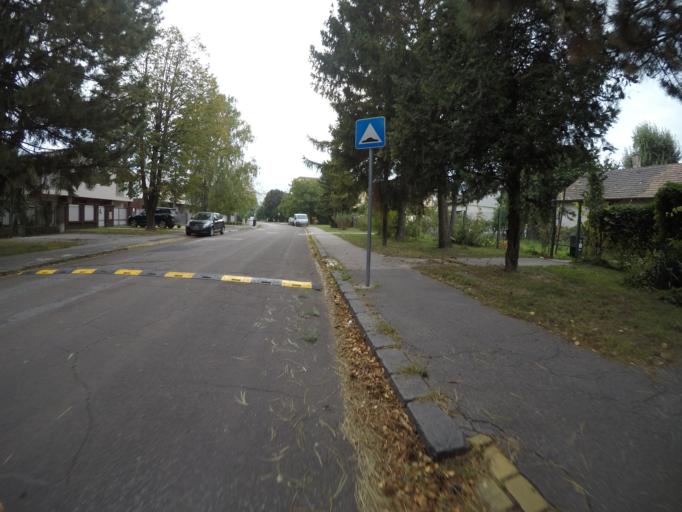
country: SK
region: Bratislavsky
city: Bratislava
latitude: 48.1679
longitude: 17.1694
